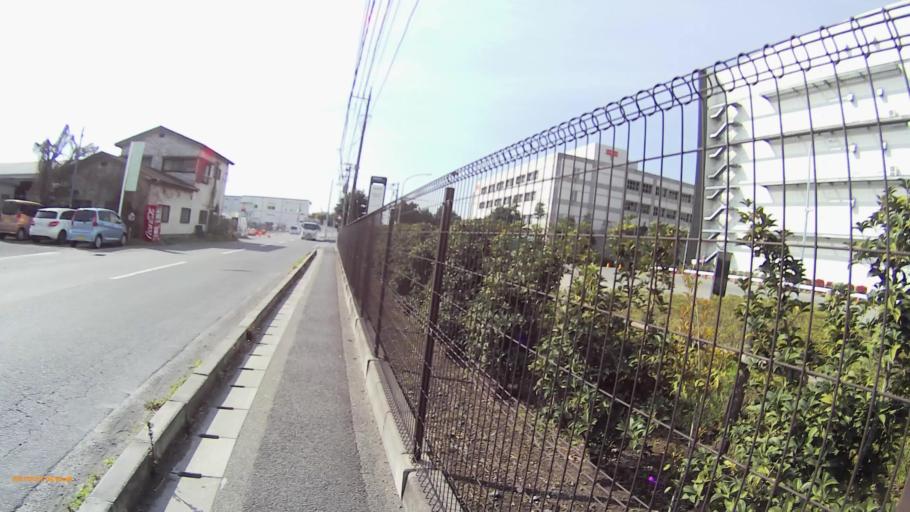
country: JP
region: Kanagawa
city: Minami-rinkan
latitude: 35.4482
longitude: 139.4164
